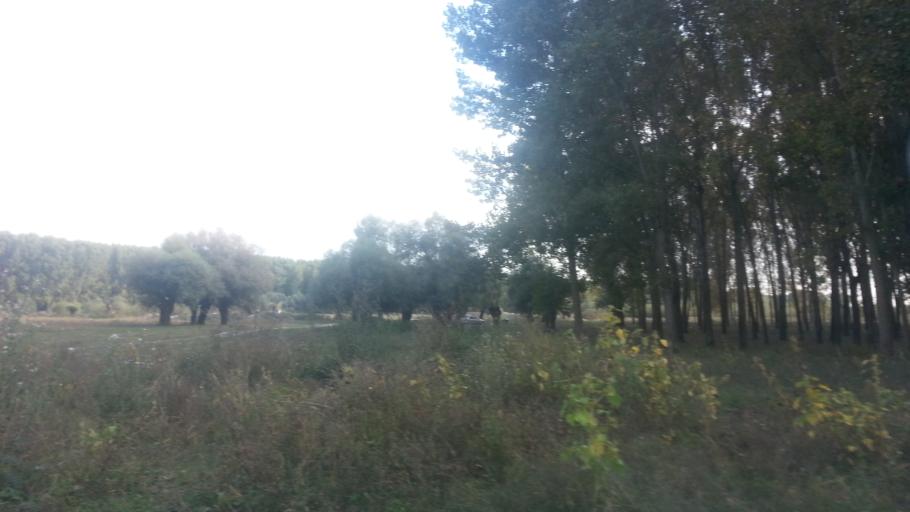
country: RS
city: Belegis
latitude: 45.0176
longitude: 20.3415
